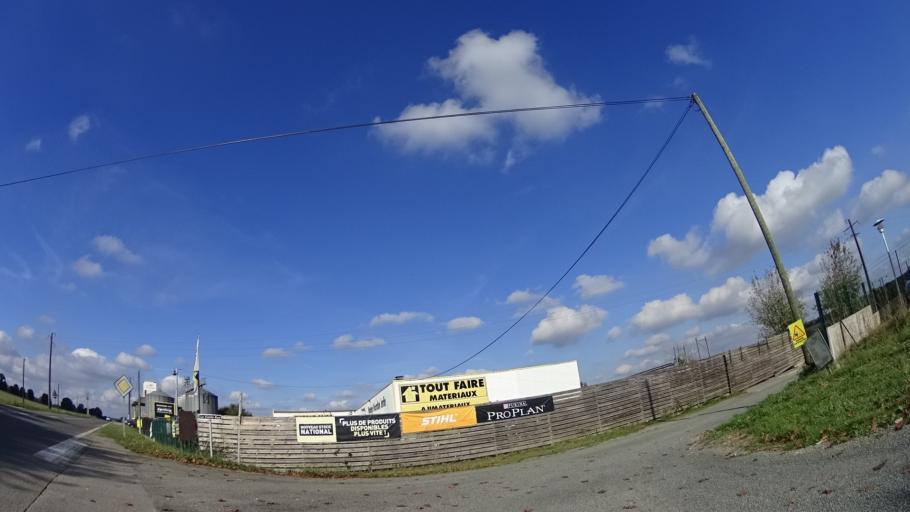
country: FR
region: Brittany
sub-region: Departement d'Ille-et-Vilaine
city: Geveze
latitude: 48.2256
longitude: -1.7959
